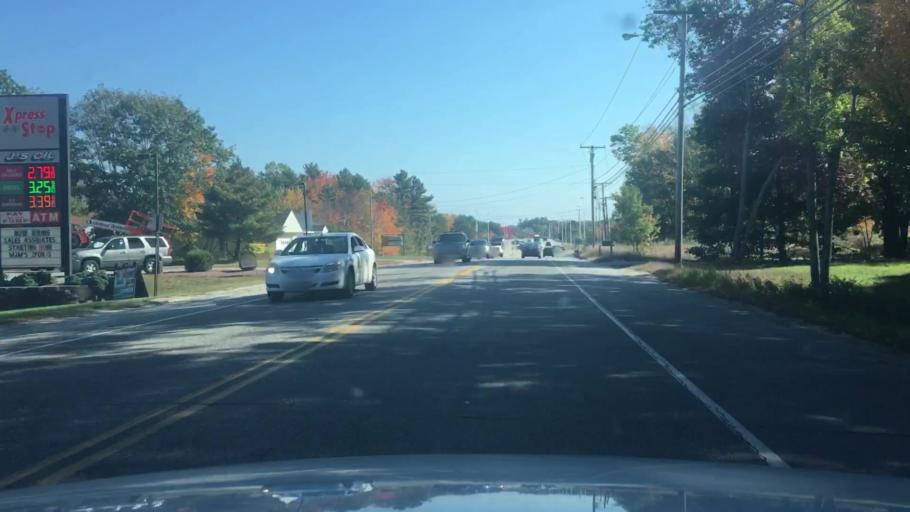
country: US
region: Maine
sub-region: Sagadahoc County
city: Topsham
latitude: 43.9448
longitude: -69.9837
